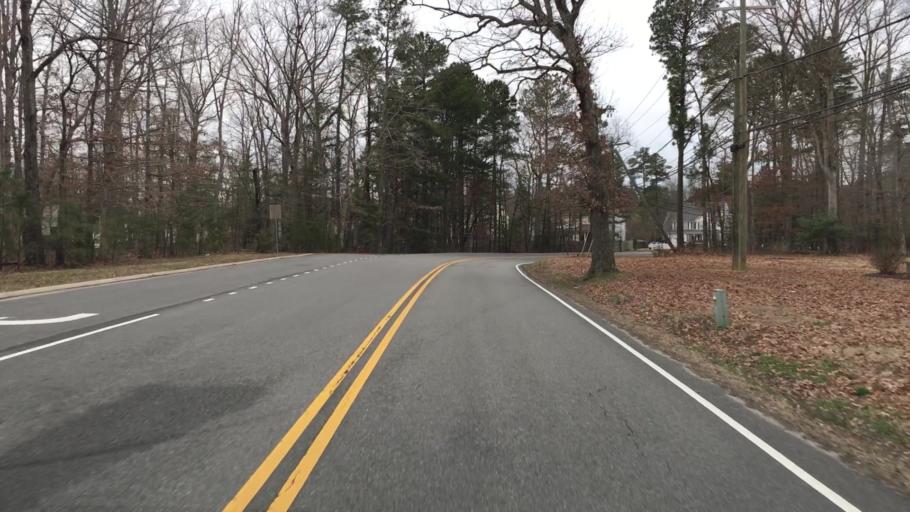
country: US
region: Virginia
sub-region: Henrico County
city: Glen Allen
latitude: 37.6695
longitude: -77.5575
